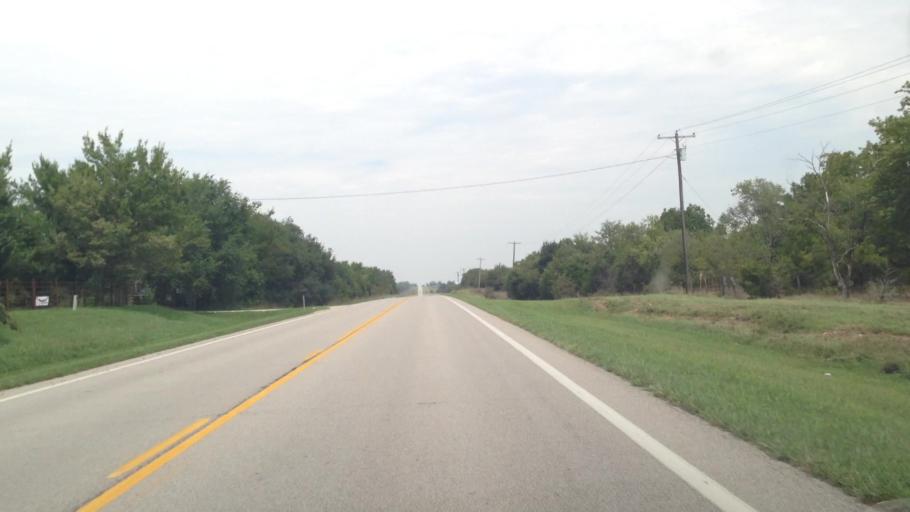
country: US
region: Kansas
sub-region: Neosho County
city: Erie
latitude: 37.6523
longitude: -95.2516
